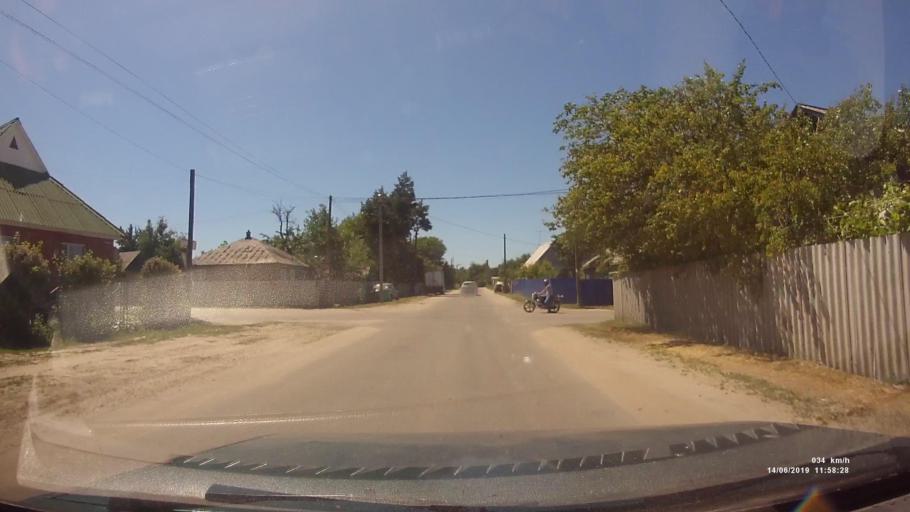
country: RU
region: Rostov
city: Kazanskaya
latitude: 49.7960
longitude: 41.1419
